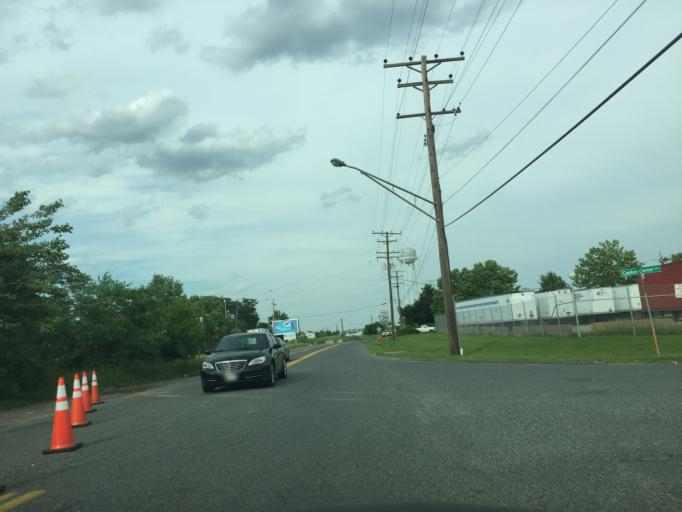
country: US
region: Maryland
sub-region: Baltimore County
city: Rosedale
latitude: 39.3006
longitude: -76.5170
